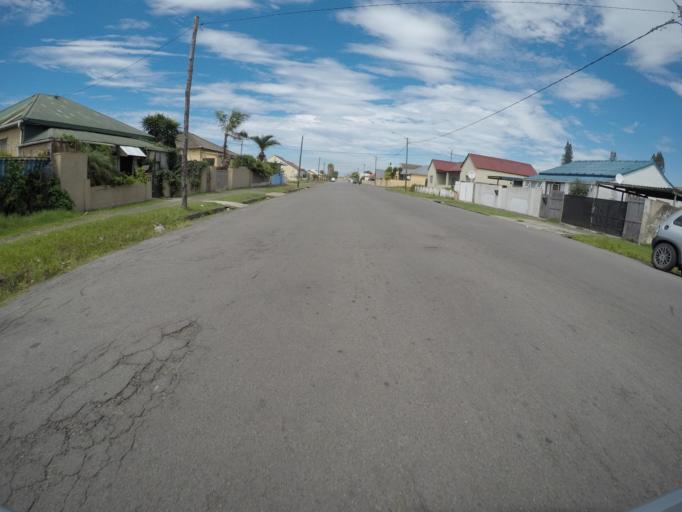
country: ZA
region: Eastern Cape
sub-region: Buffalo City Metropolitan Municipality
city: East London
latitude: -33.0346
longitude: 27.9070
